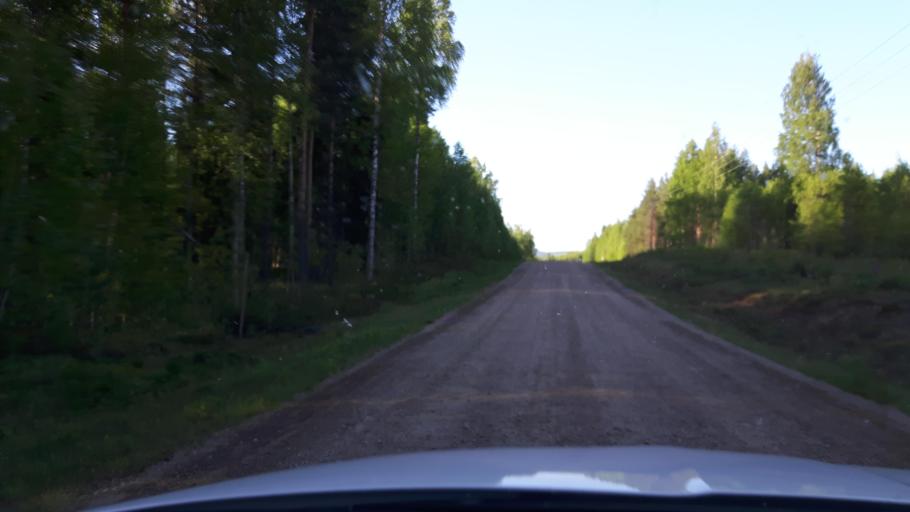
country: SE
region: Vaesternorrland
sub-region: Ange Kommun
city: Ange
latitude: 62.1621
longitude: 15.6592
